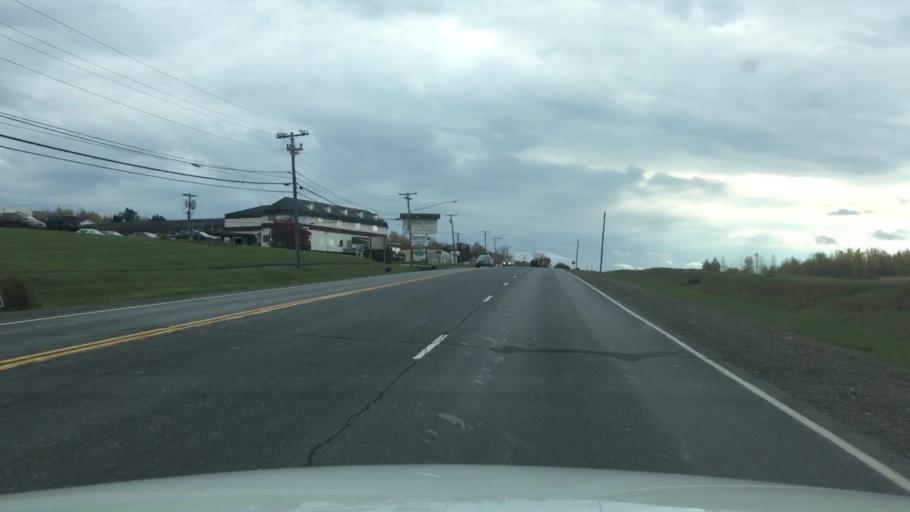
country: US
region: Maine
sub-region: Aroostook County
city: Presque Isle
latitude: 46.6690
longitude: -68.0129
